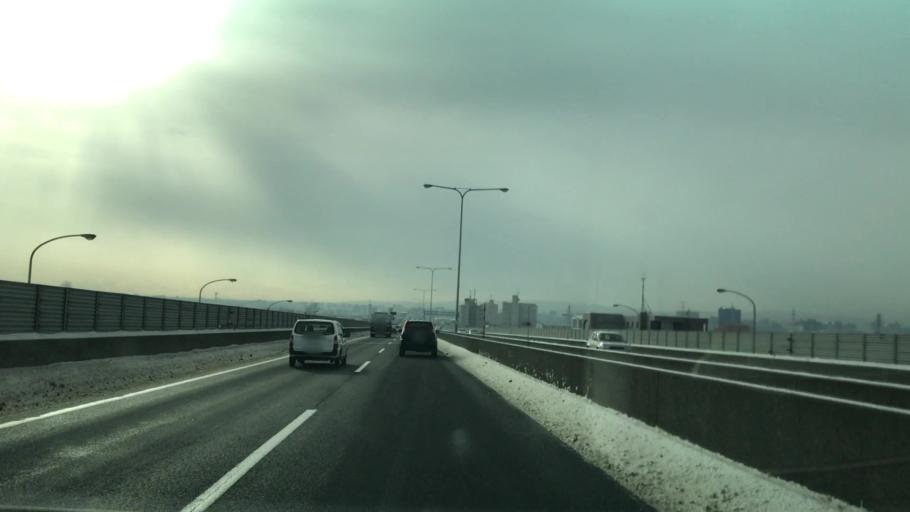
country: JP
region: Hokkaido
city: Sapporo
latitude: 43.0718
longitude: 141.4219
